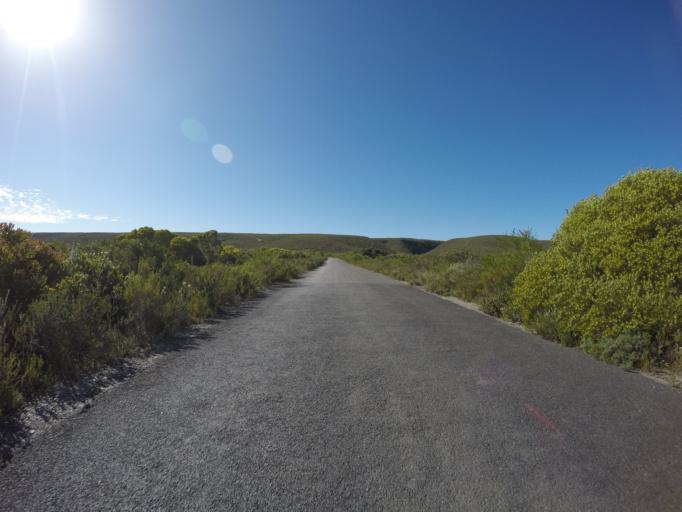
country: ZA
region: Western Cape
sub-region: Overberg District Municipality
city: Bredasdorp
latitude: -34.4318
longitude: 20.4181
